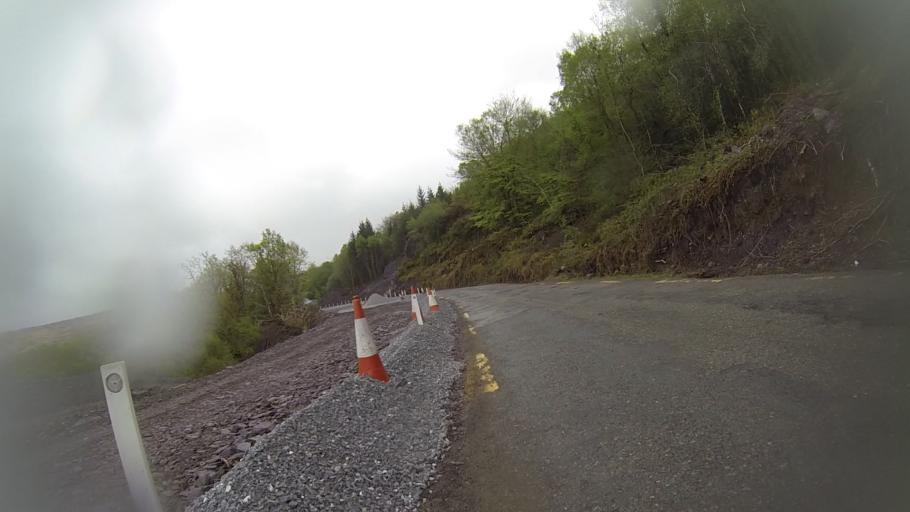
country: IE
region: Munster
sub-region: Ciarrai
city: Kenmare
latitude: 51.8076
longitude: -9.5605
